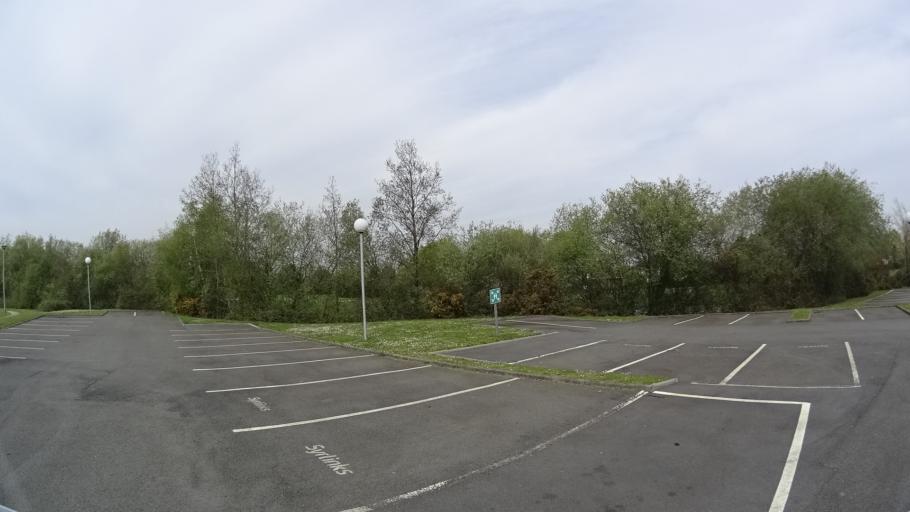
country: FR
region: Brittany
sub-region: Departement d'Ille-et-Vilaine
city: Bruz
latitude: 48.0344
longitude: -1.7604
